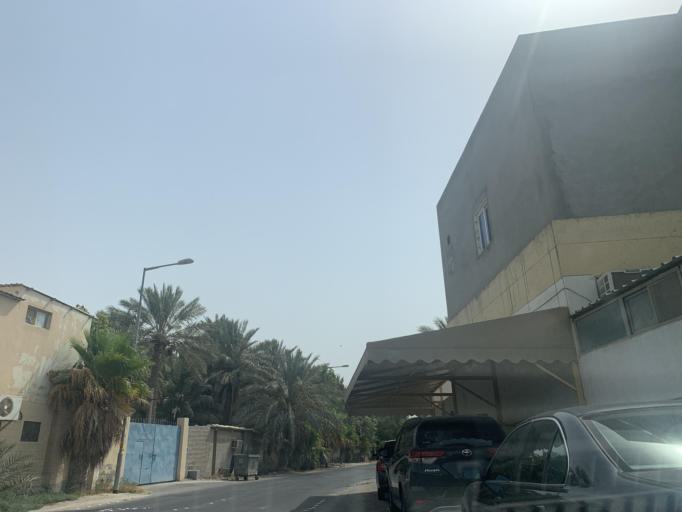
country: BH
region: Manama
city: Jidd Hafs
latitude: 26.1974
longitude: 50.4672
